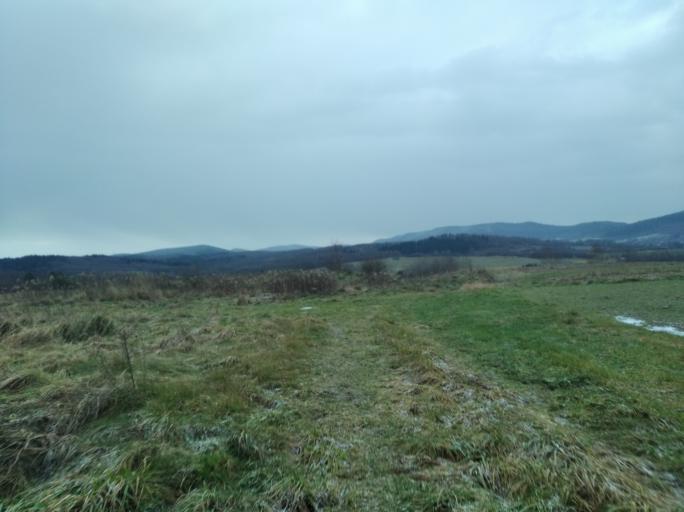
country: PL
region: Subcarpathian Voivodeship
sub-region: Powiat strzyzowski
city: Wysoka Strzyzowska
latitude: 49.8318
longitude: 21.7540
